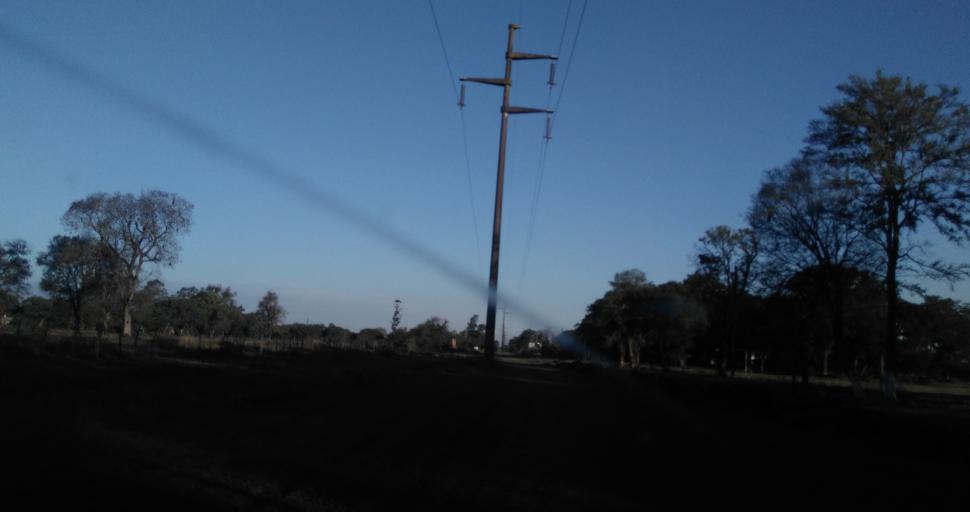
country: AR
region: Chaco
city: Fontana
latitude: -27.3965
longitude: -59.0052
